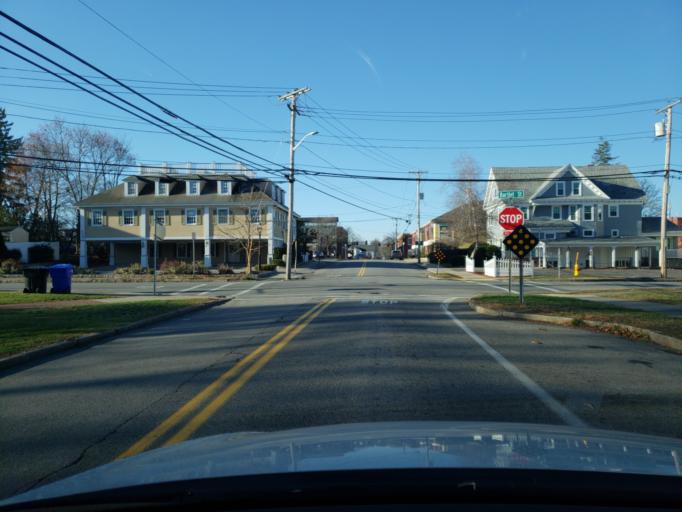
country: US
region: Massachusetts
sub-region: Essex County
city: Andover
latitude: 42.6559
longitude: -71.1378
